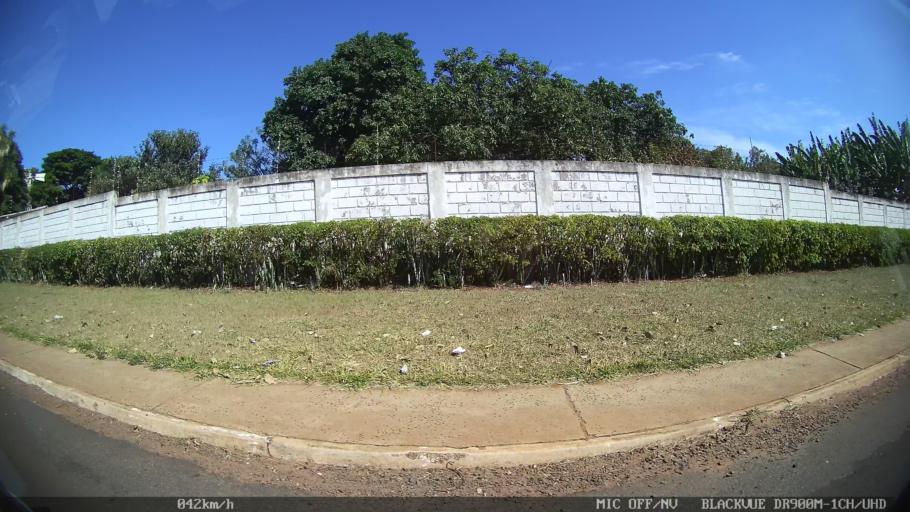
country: BR
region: Sao Paulo
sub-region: Franca
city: Franca
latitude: -20.5427
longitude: -47.4592
